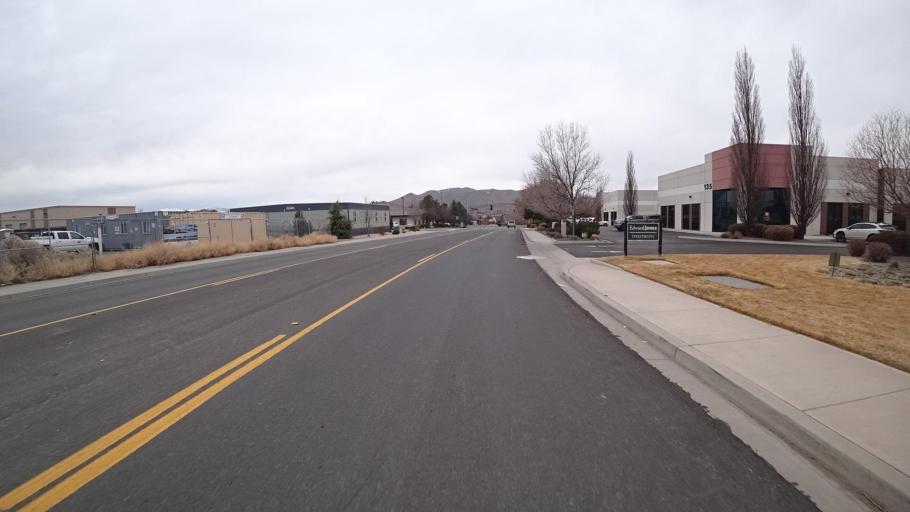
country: US
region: Nevada
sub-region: Washoe County
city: Spanish Springs
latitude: 39.6693
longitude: -119.7057
